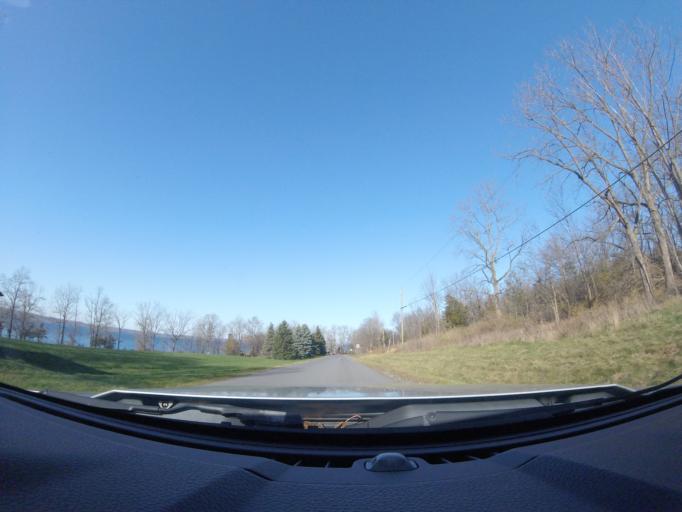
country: US
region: New York
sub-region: Cayuga County
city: Union Springs
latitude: 42.7167
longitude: -76.7071
